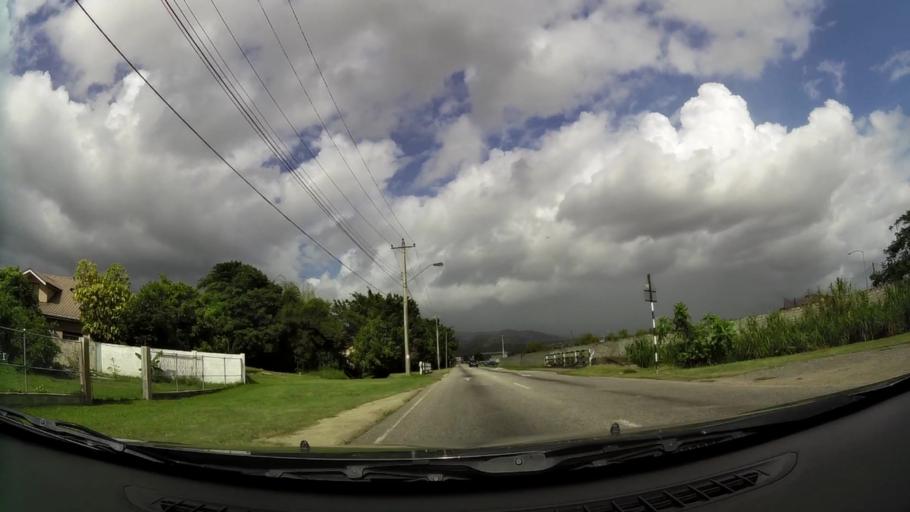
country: TT
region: Tunapuna/Piarco
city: Arouca
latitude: 10.6303
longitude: -61.3516
